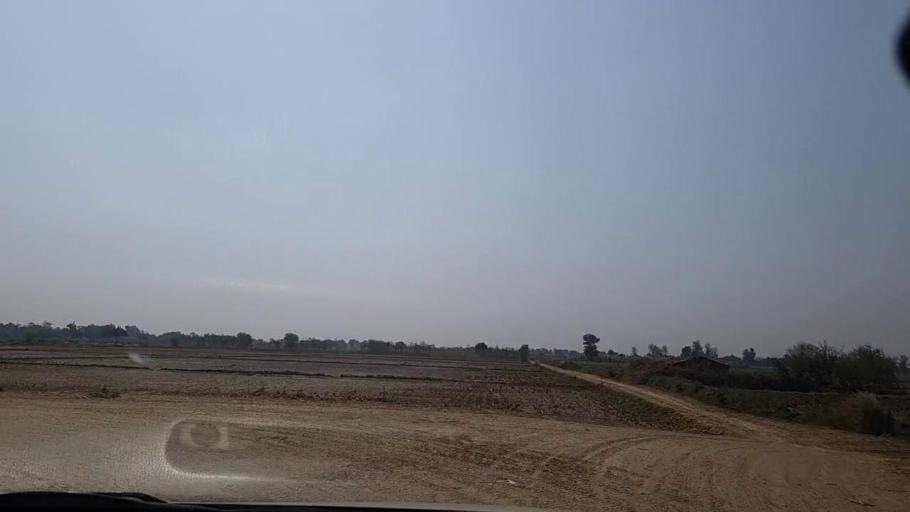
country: PK
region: Sindh
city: Mirpur Khas
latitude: 25.4826
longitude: 69.1935
